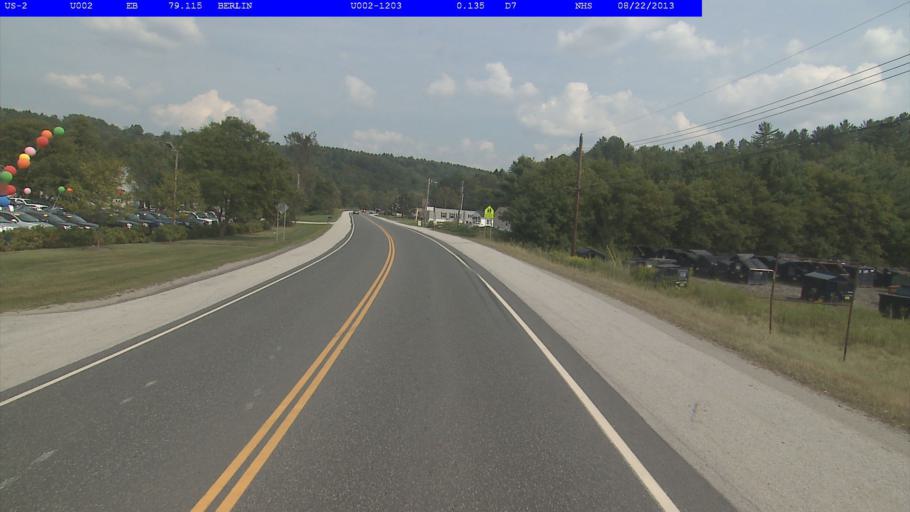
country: US
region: Vermont
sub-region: Washington County
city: Montpelier
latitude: 44.2413
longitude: -72.5404
